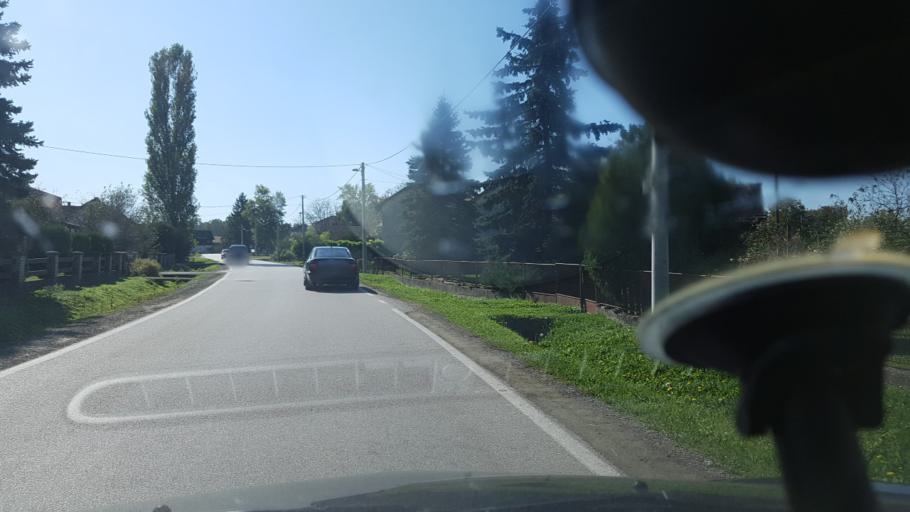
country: HR
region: Zagrebacka
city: Lupoglav
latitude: 45.7392
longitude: 16.3017
